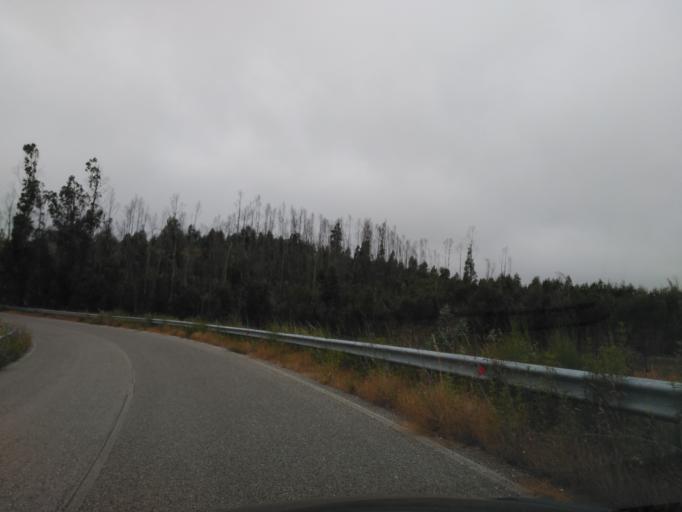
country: PT
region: Castelo Branco
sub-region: Vila de Rei
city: Vila de Rei
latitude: 39.5901
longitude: -8.1033
